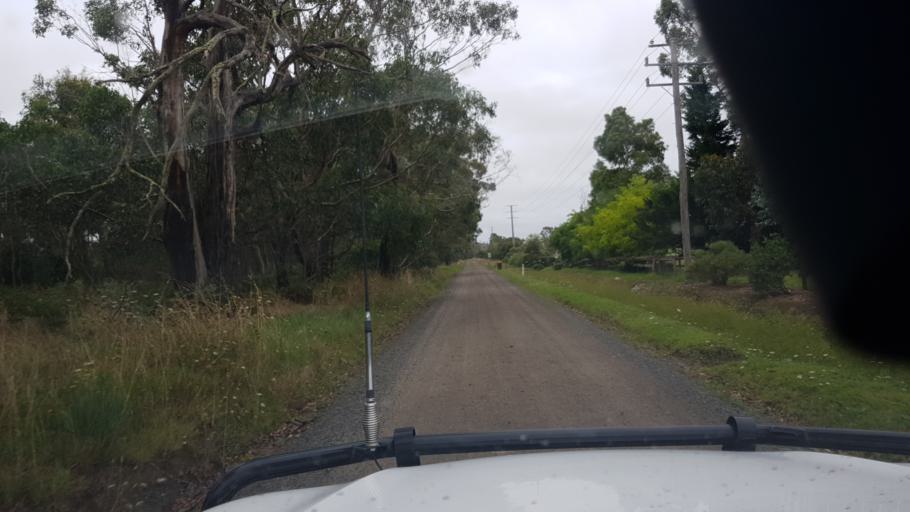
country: AU
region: Victoria
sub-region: Cardinia
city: Bunyip
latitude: -38.1067
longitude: 145.7586
